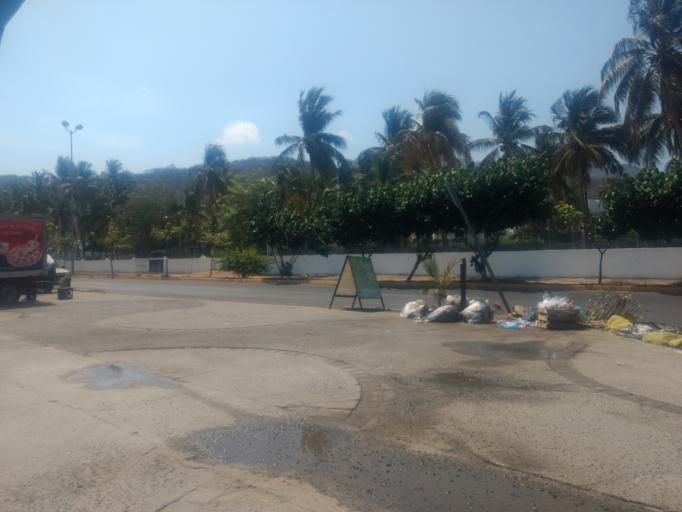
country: MX
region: Colima
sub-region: Manzanillo
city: Manzanillo
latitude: 19.1203
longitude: -104.3781
